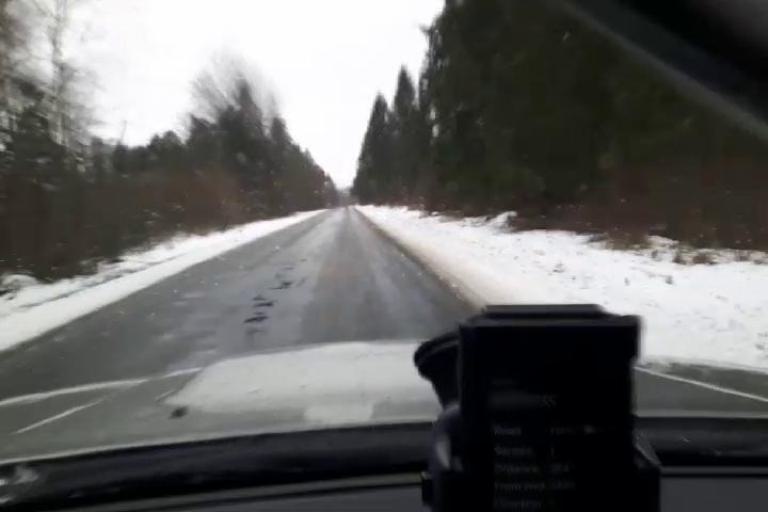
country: EE
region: Harju
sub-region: Harku vald
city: Tabasalu
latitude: 59.4295
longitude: 24.4599
